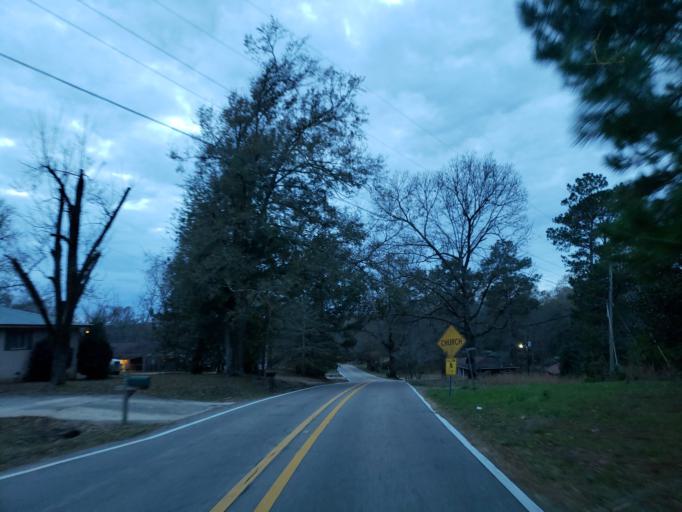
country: US
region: Mississippi
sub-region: Forrest County
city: Petal
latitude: 31.3394
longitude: -89.2540
